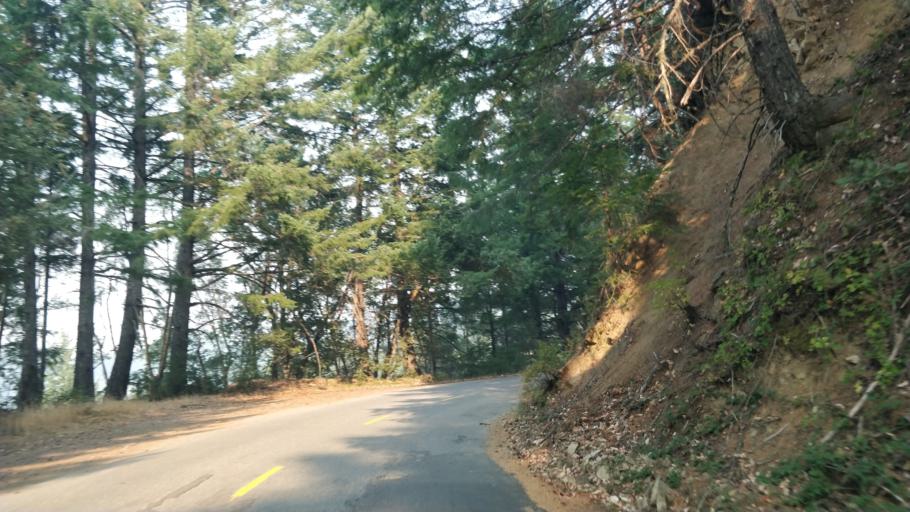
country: US
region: California
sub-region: Humboldt County
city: Rio Dell
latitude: 40.2844
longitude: -124.0635
